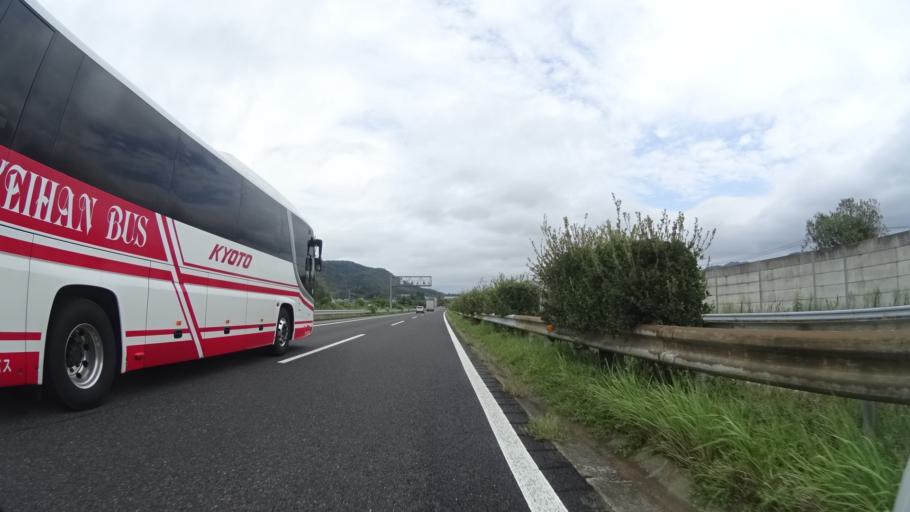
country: JP
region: Hyogo
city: Ono
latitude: 34.9407
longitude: 134.8208
